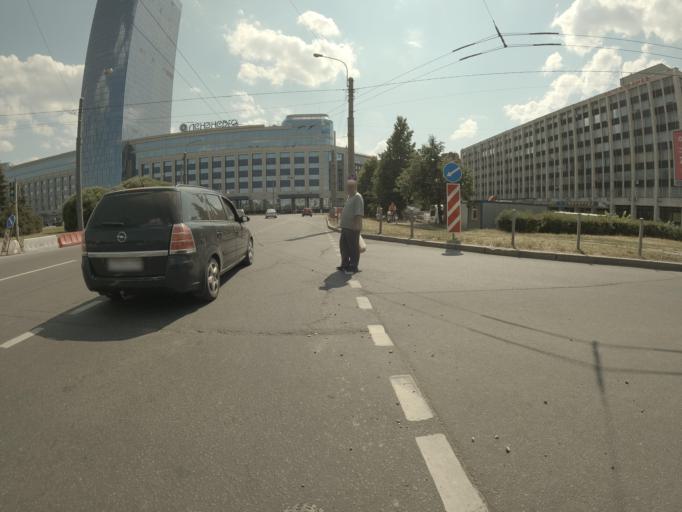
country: RU
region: St.-Petersburg
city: Avtovo
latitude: 59.8518
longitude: 30.3029
